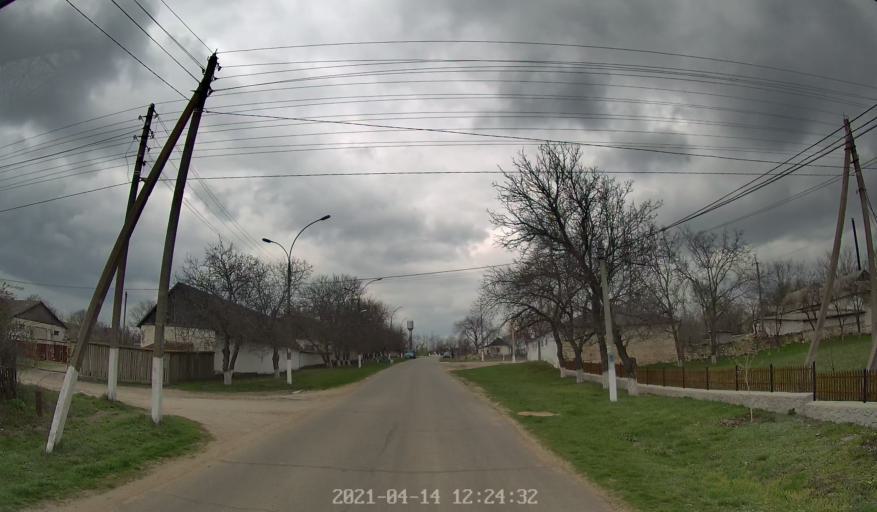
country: MD
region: Criuleni
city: Criuleni
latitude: 47.1708
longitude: 29.1946
